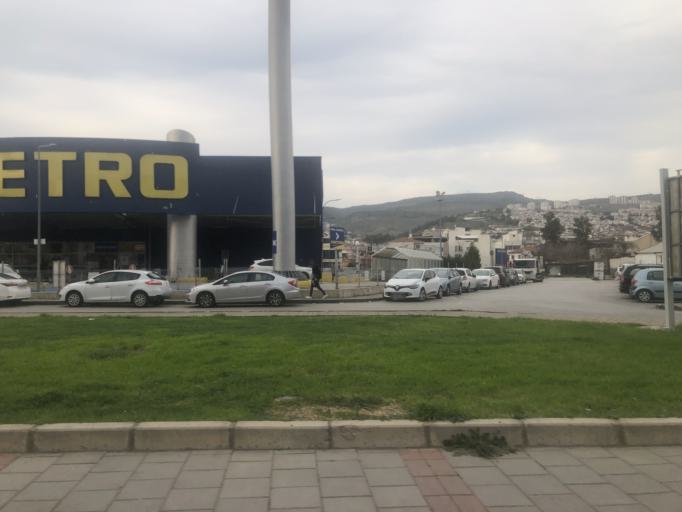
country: TR
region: Izmir
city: Karsiyaka
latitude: 38.4888
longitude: 27.0715
